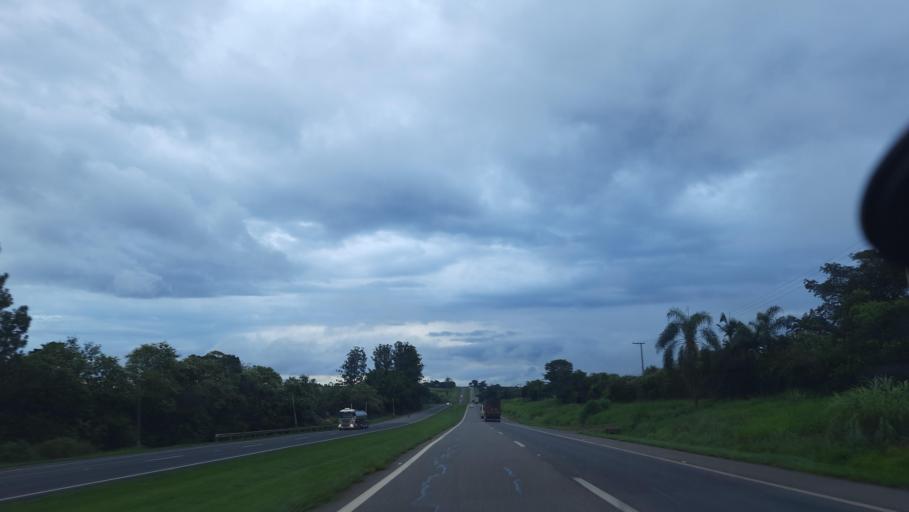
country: BR
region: Sao Paulo
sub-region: Moji-Guacu
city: Mogi-Gaucu
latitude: -22.2382
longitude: -46.9784
